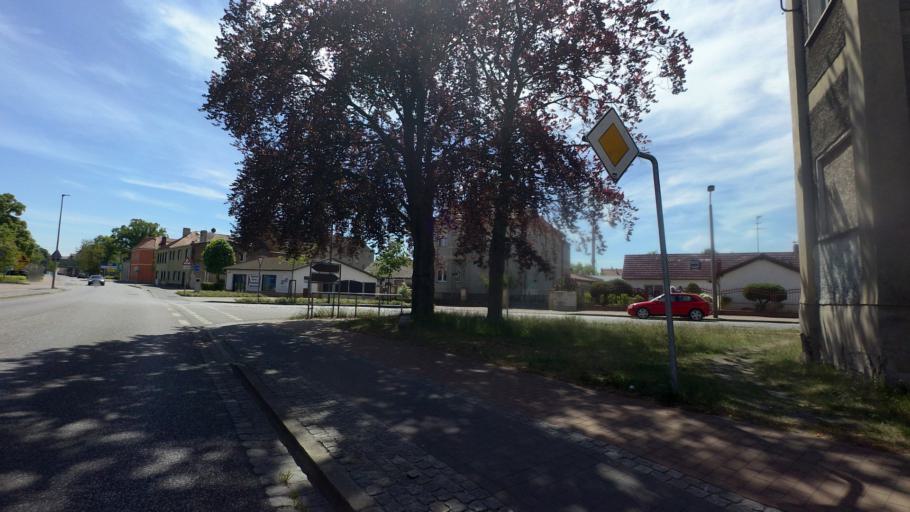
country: DE
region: Brandenburg
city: Luckenwalde
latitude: 52.0966
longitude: 13.1631
